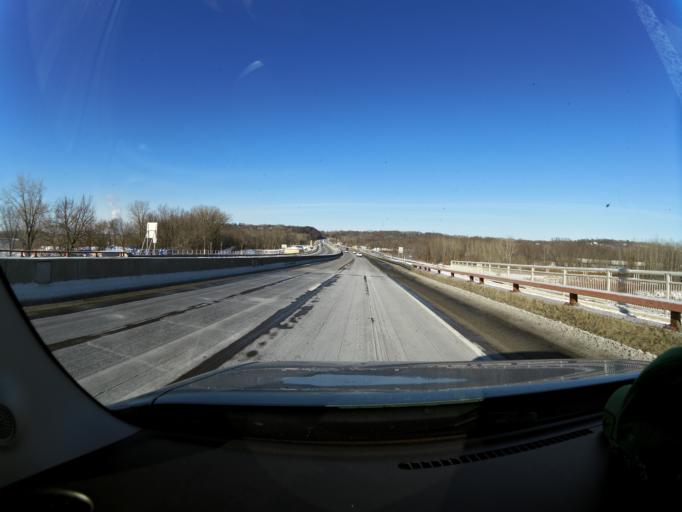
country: US
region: Minnesota
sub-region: Dakota County
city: Hastings
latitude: 44.7490
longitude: -92.8527
